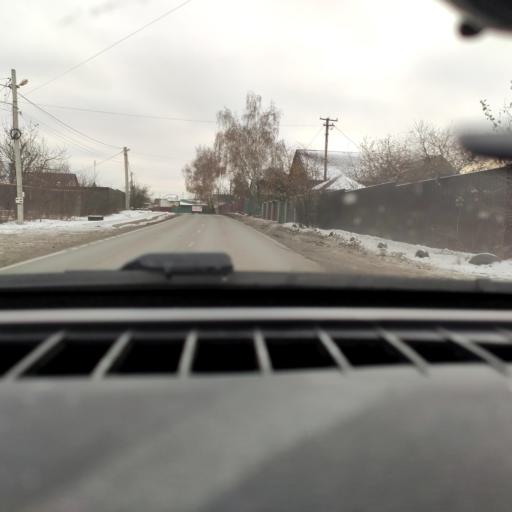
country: RU
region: Voronezj
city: Podgornoye
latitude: 51.7987
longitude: 39.1446
